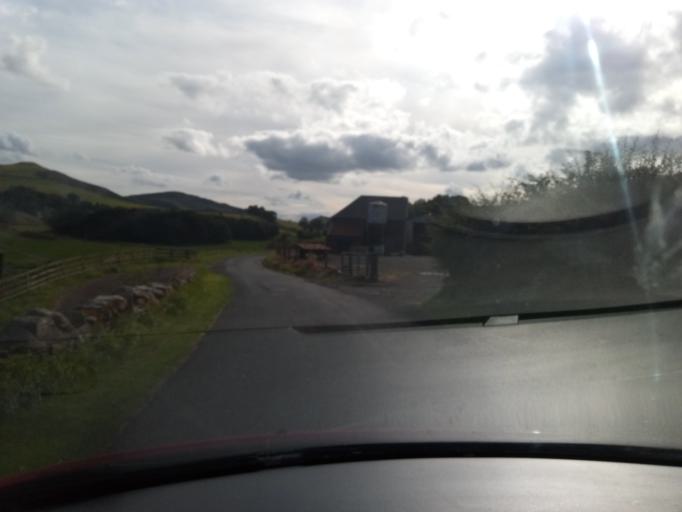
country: GB
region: Scotland
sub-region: The Scottish Borders
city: Kelso
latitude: 55.4825
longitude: -2.3513
